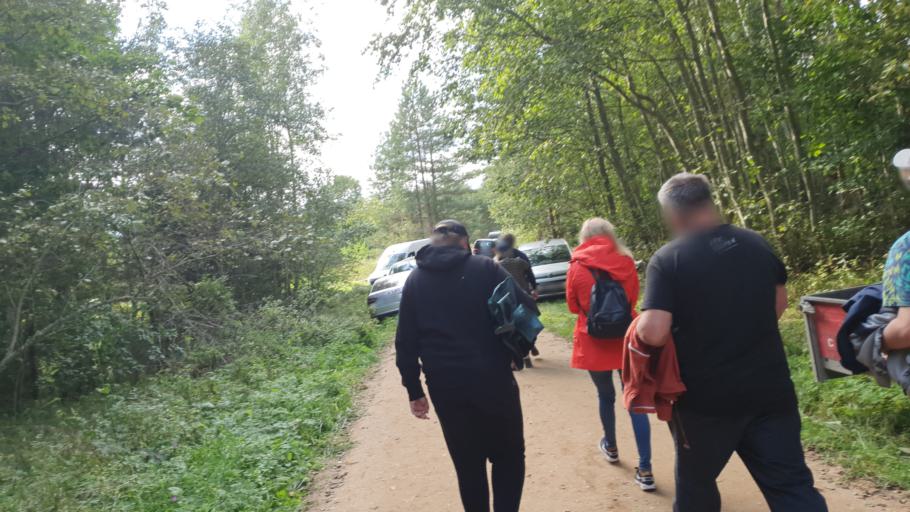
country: EE
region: Tartu
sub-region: UElenurme vald
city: Ulenurme
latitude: 58.1331
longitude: 26.7726
